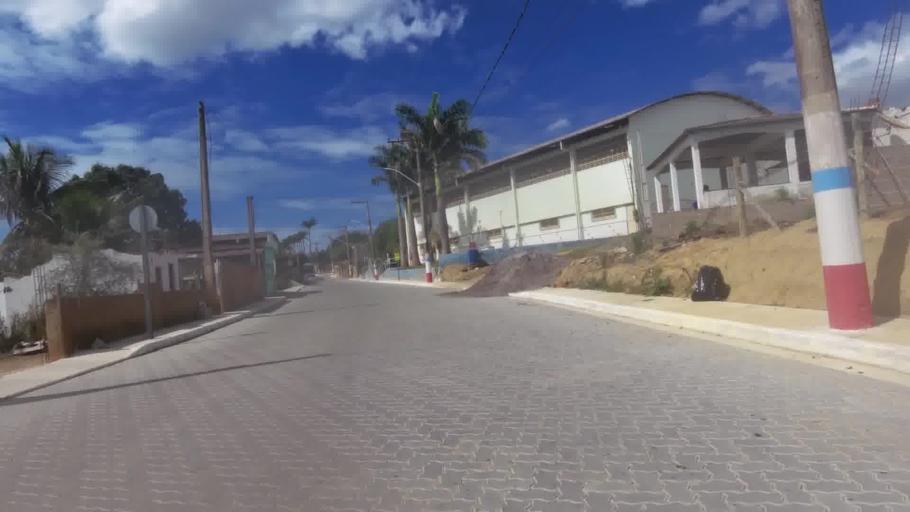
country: BR
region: Espirito Santo
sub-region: Marataizes
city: Marataizes
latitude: -21.1792
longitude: -40.9869
